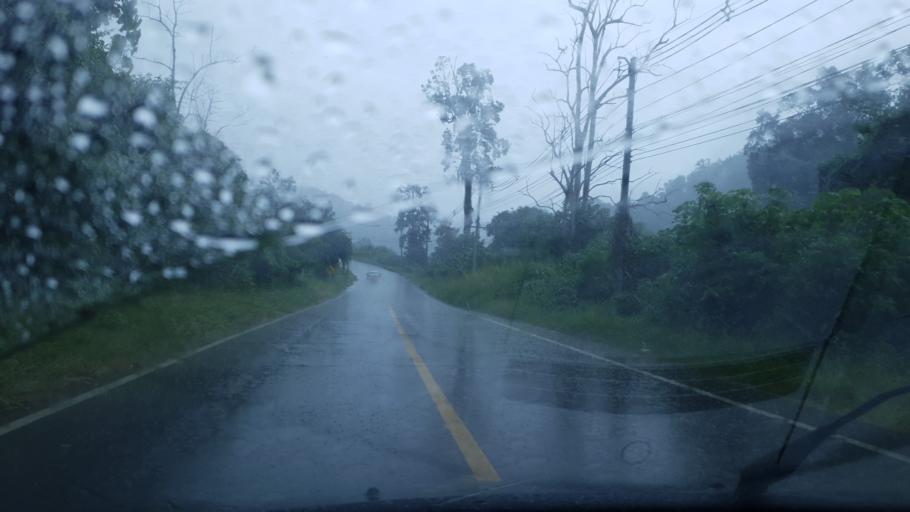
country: TH
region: Mae Hong Son
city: Khun Yuam
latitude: 18.6507
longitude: 97.9322
